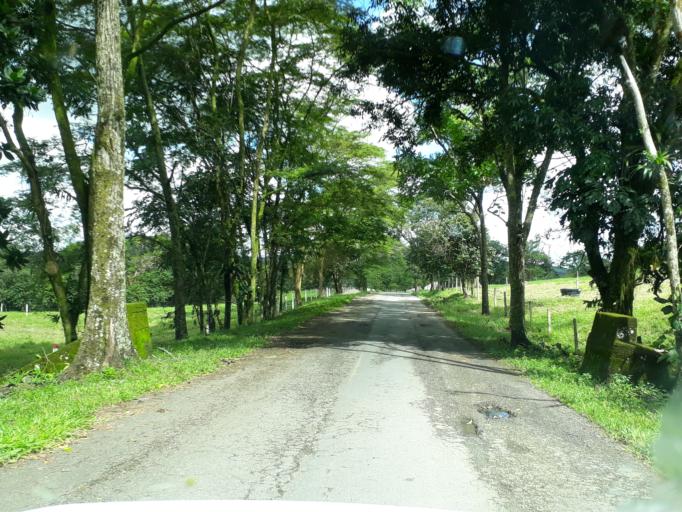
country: CO
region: Cundinamarca
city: Medina
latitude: 4.5518
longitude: -73.3603
